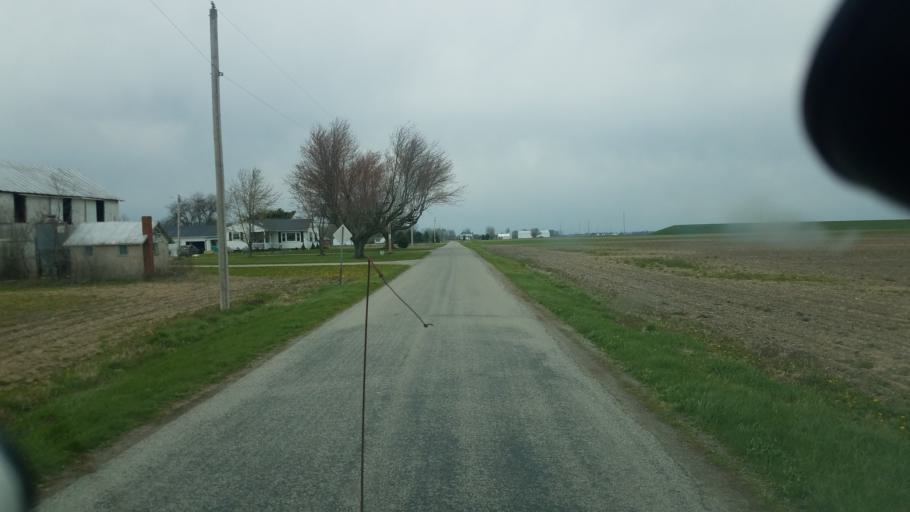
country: US
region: Ohio
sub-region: Union County
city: Richwood
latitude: 40.3825
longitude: -83.2500
